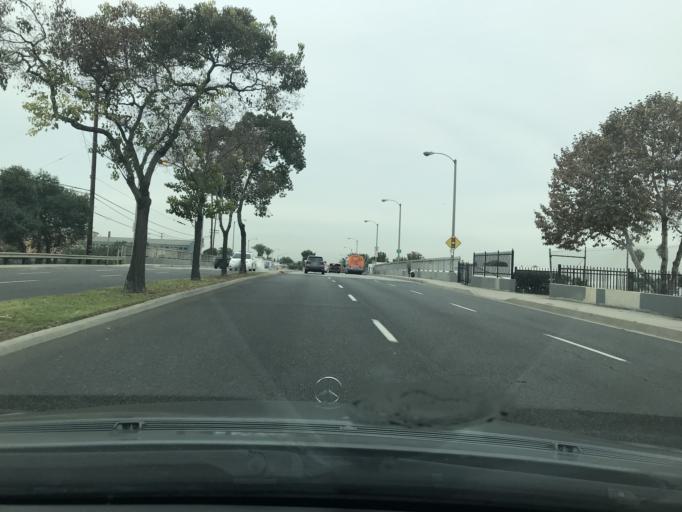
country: US
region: California
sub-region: Los Angeles County
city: Bell Gardens
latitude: 33.9604
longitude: -118.1434
